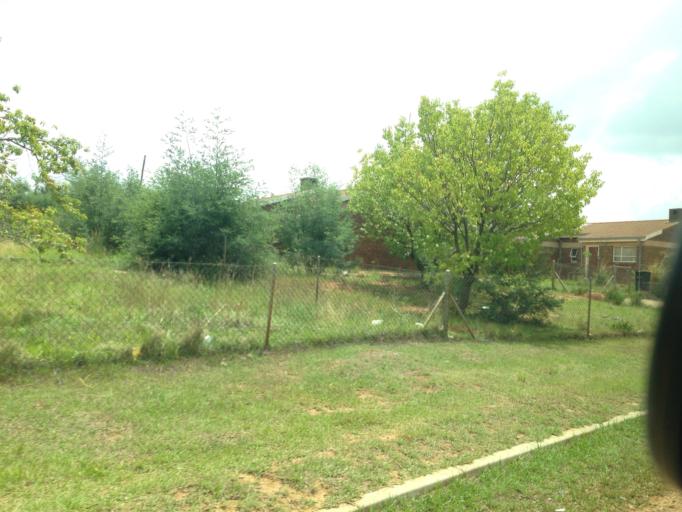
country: LS
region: Maseru
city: Maseru
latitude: -29.4536
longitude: 27.5621
